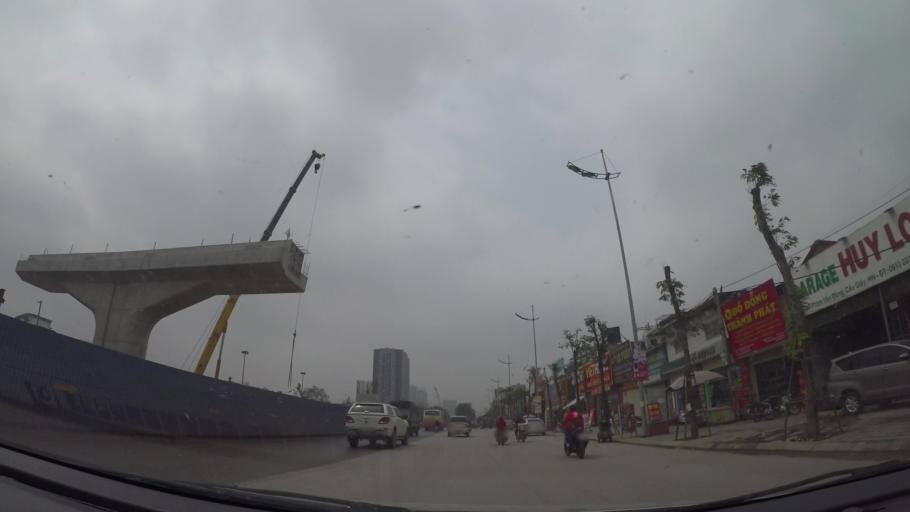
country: VN
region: Ha Noi
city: Cau Dien
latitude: 21.0474
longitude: 105.7812
